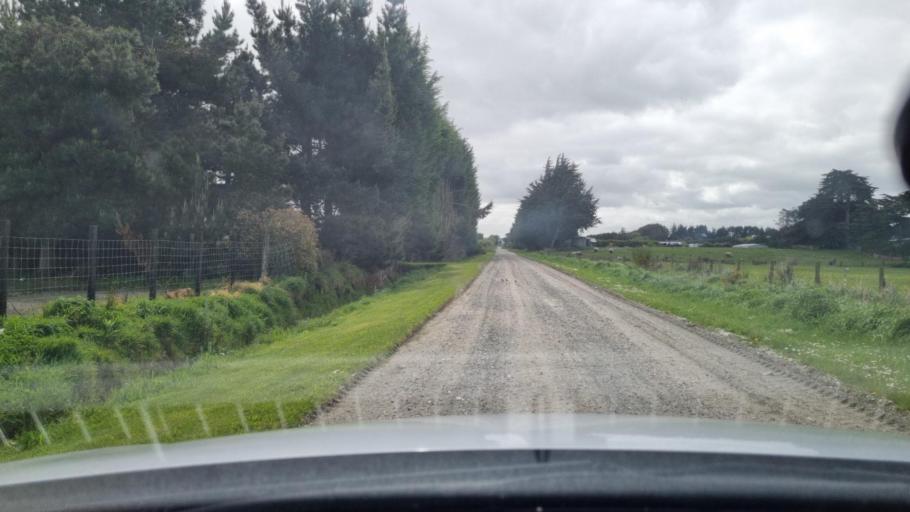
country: NZ
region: Southland
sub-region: Invercargill City
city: Invercargill
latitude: -46.4388
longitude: 168.3896
